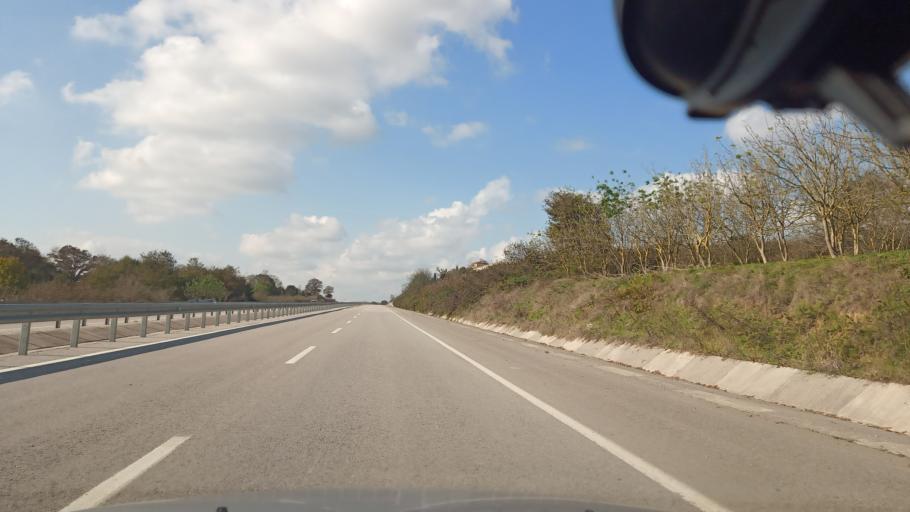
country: TR
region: Sakarya
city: Kaynarca
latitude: 41.0724
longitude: 30.3912
